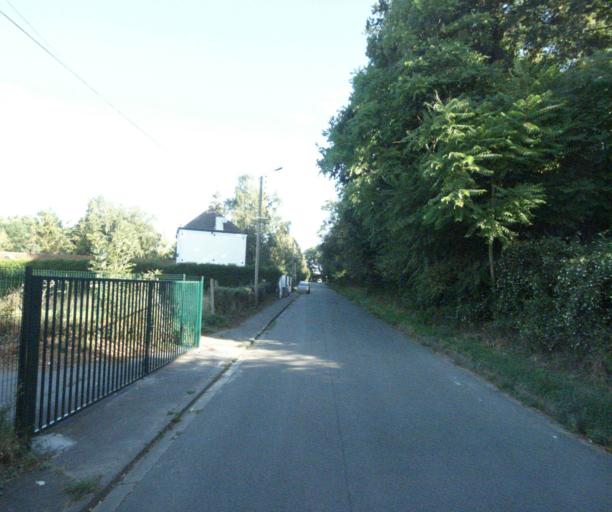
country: FR
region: Nord-Pas-de-Calais
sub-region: Departement du Nord
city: Sainghin-en-Melantois
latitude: 50.5763
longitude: 3.1894
